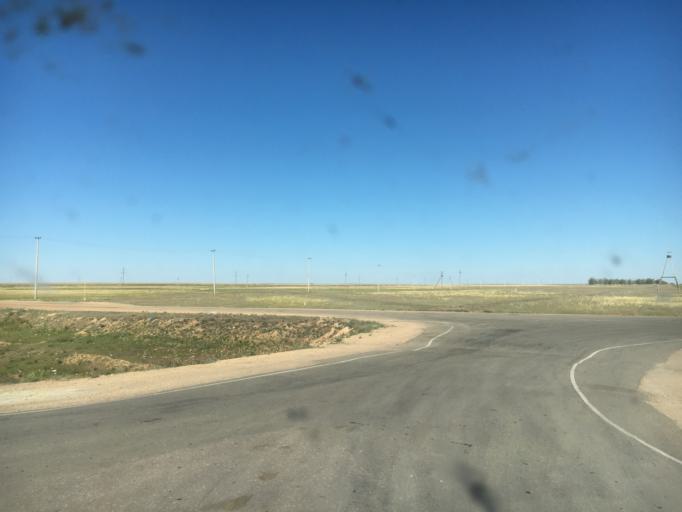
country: RU
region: Orenburg
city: Dombarovskiy
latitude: 50.0710
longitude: 59.6245
